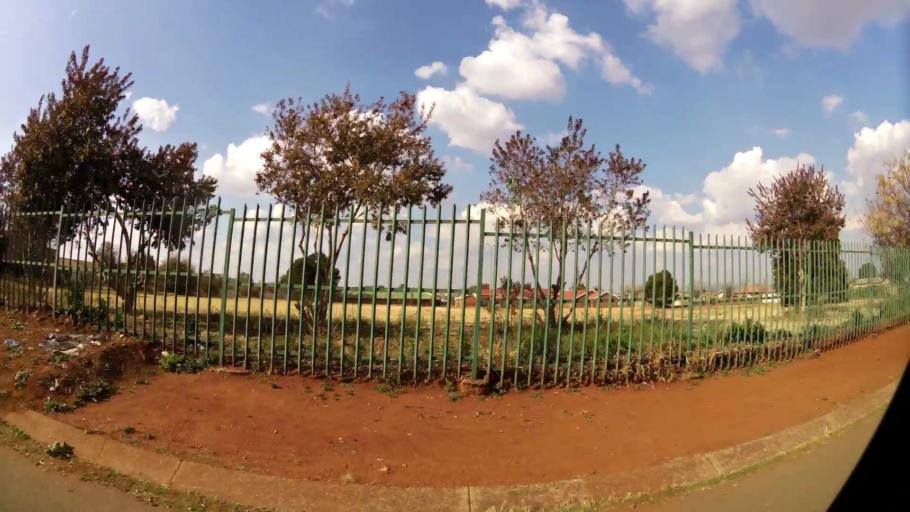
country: ZA
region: Gauteng
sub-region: City of Johannesburg Metropolitan Municipality
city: Soweto
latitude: -26.2208
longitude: 27.8646
